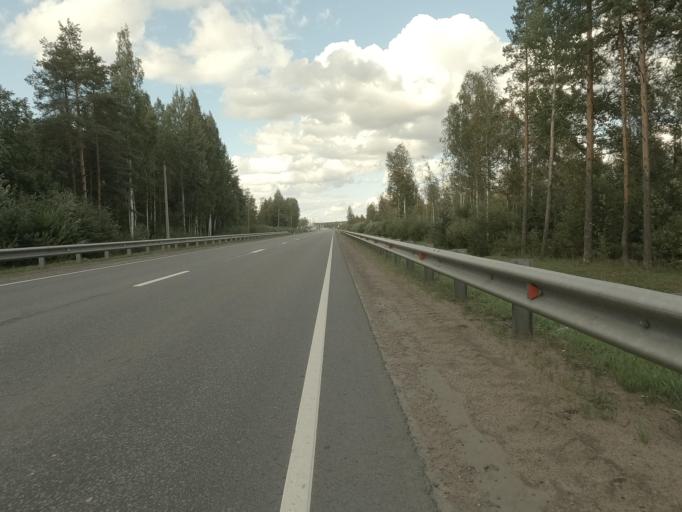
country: RU
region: Leningrad
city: Mga
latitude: 59.7418
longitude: 31.0792
